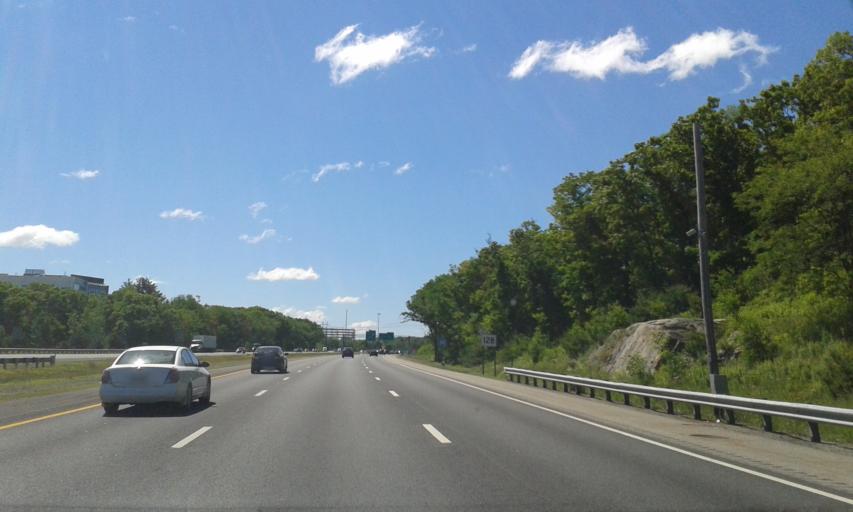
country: US
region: Massachusetts
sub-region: Middlesex County
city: Burlington
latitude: 42.4841
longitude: -71.2256
